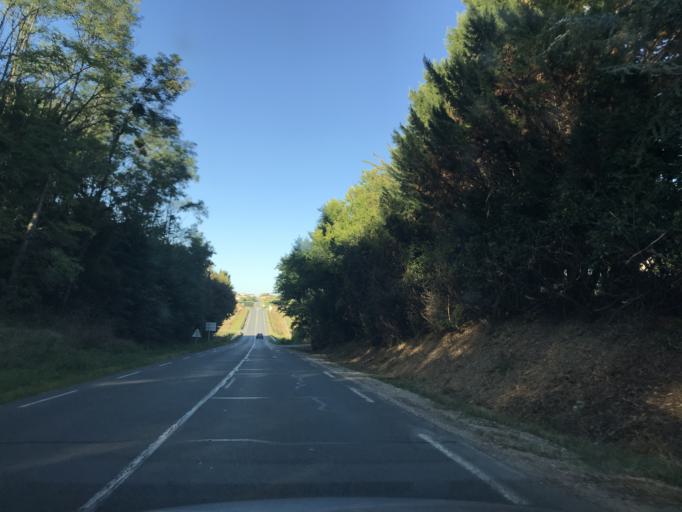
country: FR
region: Aquitaine
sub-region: Departement de la Gironde
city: Castets-en-Dorthe
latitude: 44.6253
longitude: -0.1492
